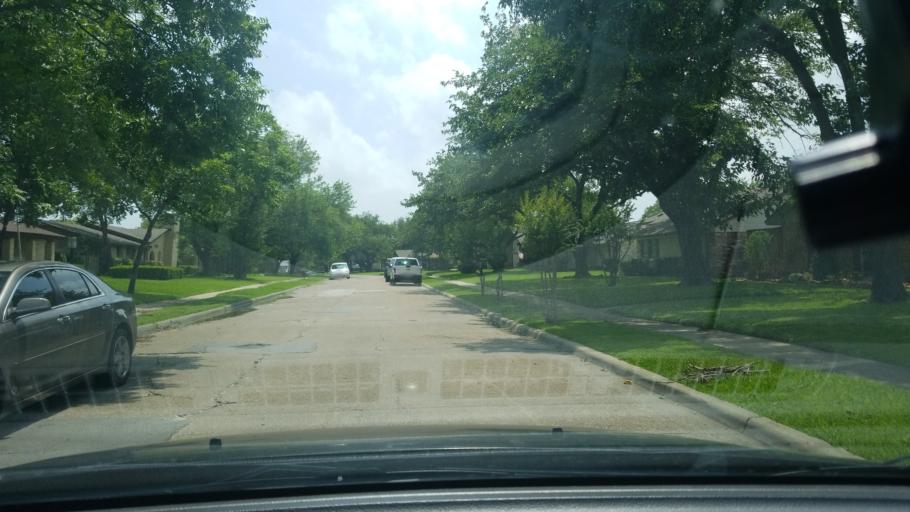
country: US
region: Texas
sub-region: Dallas County
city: Mesquite
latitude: 32.8091
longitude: -96.6463
